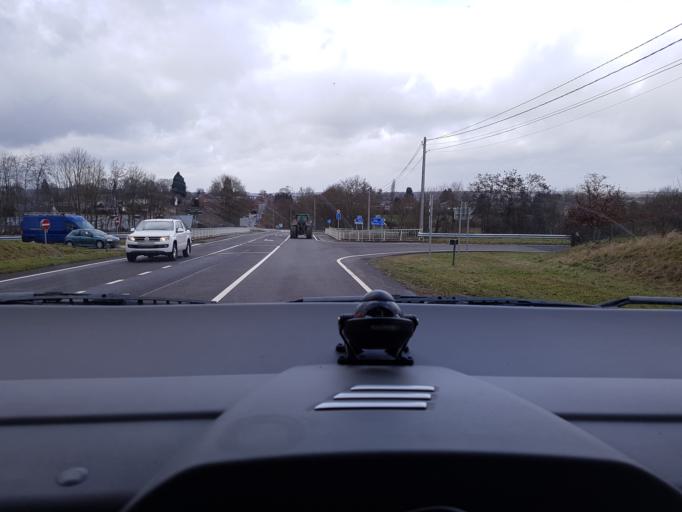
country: BE
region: Wallonia
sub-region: Province de Namur
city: Ciney
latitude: 50.2915
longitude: 5.1129
